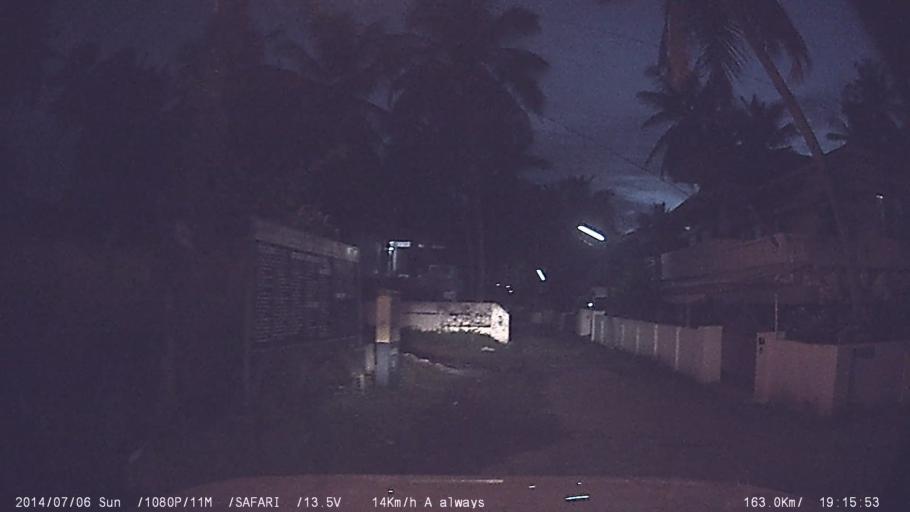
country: IN
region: Kerala
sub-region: Palakkad district
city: Palakkad
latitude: 10.7702
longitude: 76.6676
